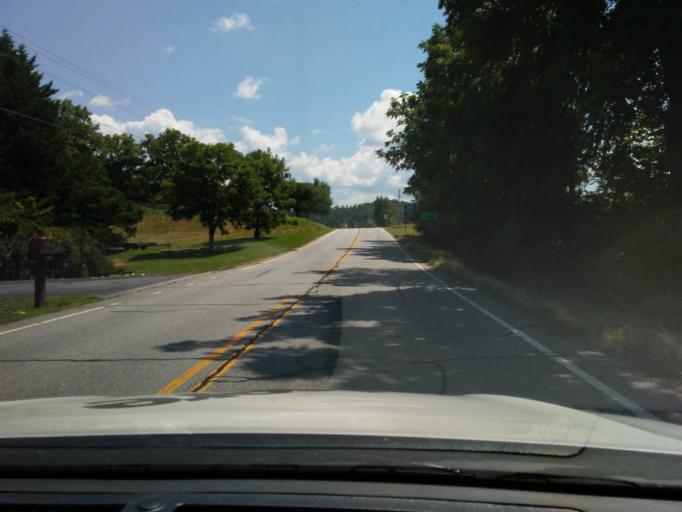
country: US
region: Georgia
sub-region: Towns County
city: Hiawassee
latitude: 34.9839
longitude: -83.7551
